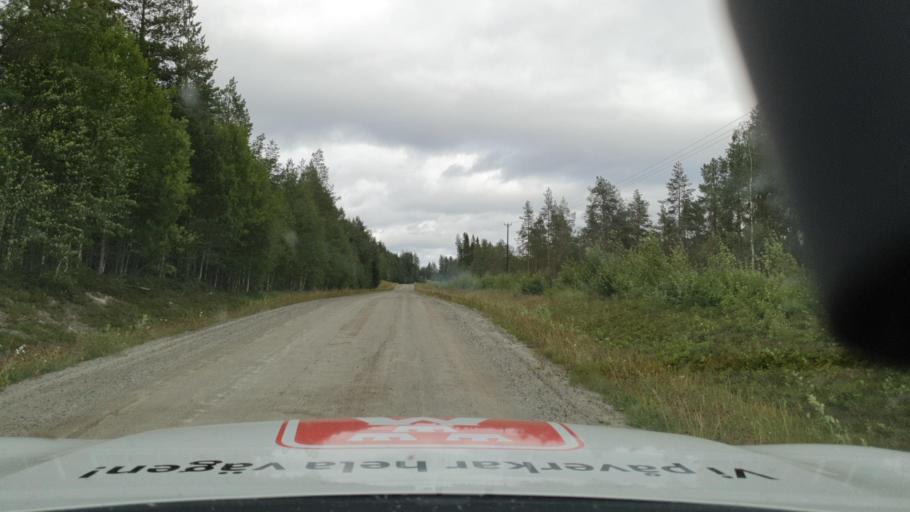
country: SE
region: Vaesterbotten
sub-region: Dorotea Kommun
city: Dorotea
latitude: 64.2020
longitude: 16.6938
